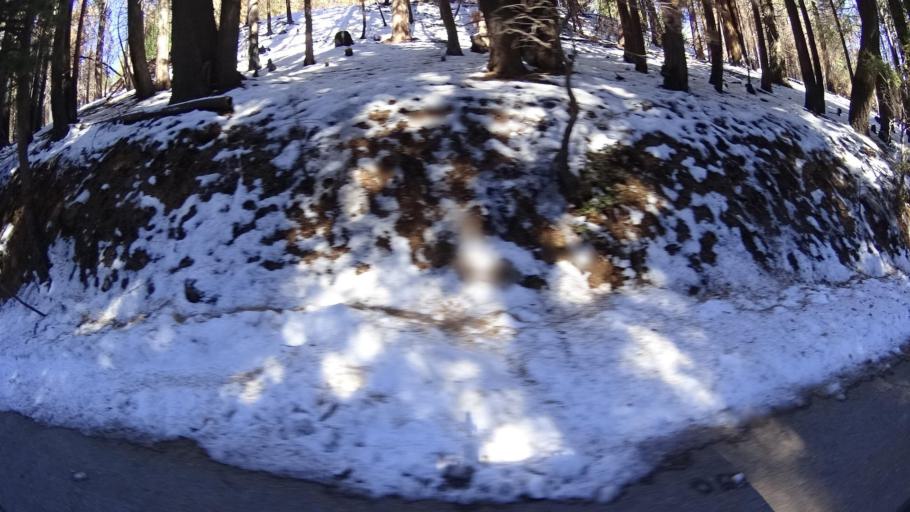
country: US
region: California
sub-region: Kern County
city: Alta Sierra
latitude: 35.7143
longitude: -118.5563
